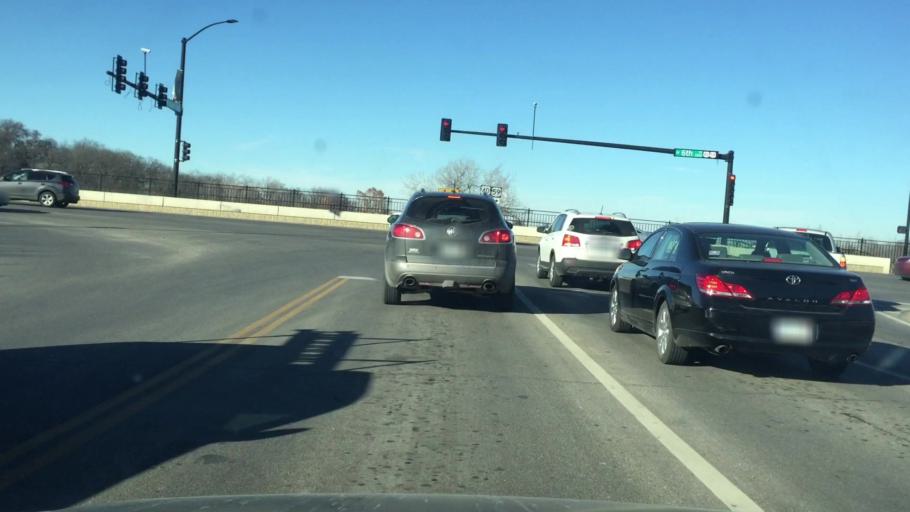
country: US
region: Kansas
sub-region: Douglas County
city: Lawrence
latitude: 38.9726
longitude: -95.2606
